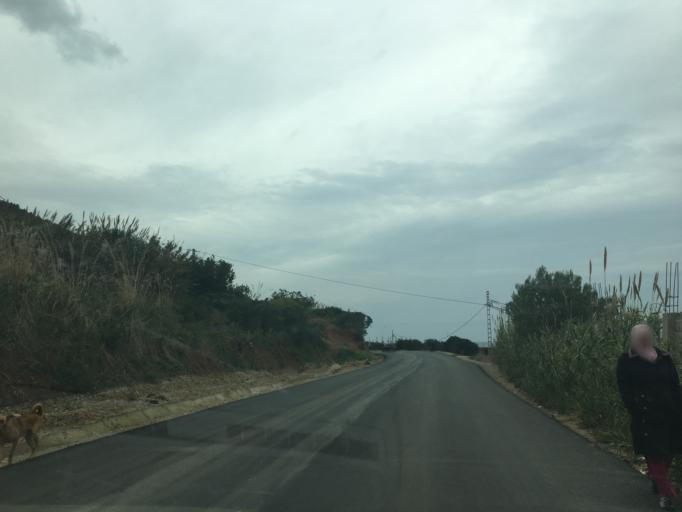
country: DZ
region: Tipaza
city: Tipasa
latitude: 36.6364
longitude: 2.3138
